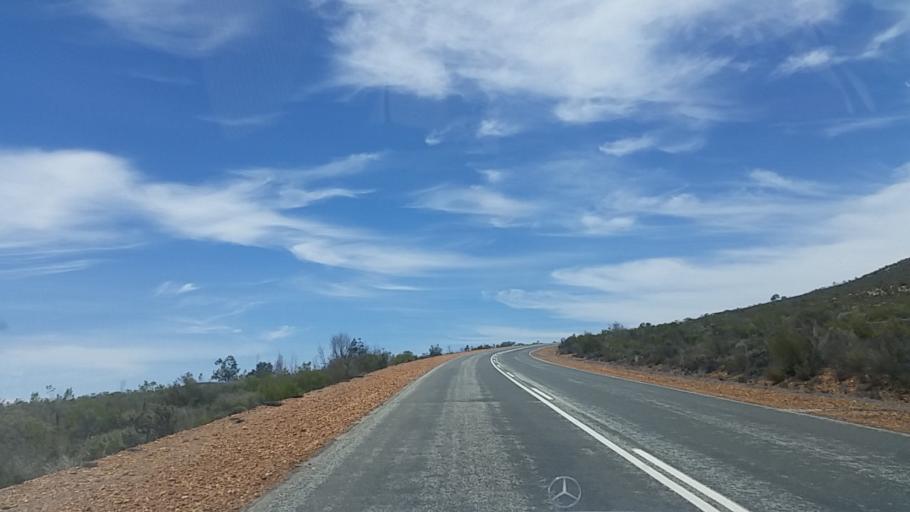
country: ZA
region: Western Cape
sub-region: Eden District Municipality
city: Knysna
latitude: -33.7126
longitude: 23.0483
